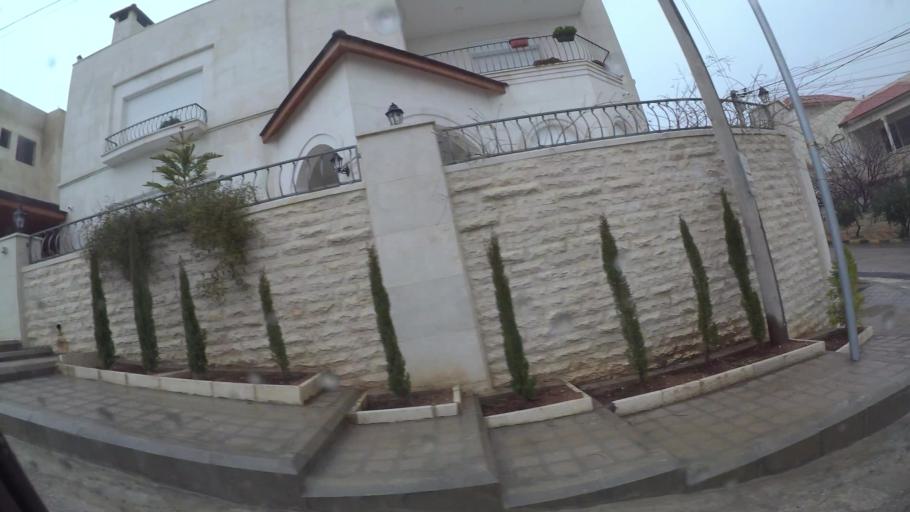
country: JO
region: Amman
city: Al Jubayhah
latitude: 32.0146
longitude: 35.8383
